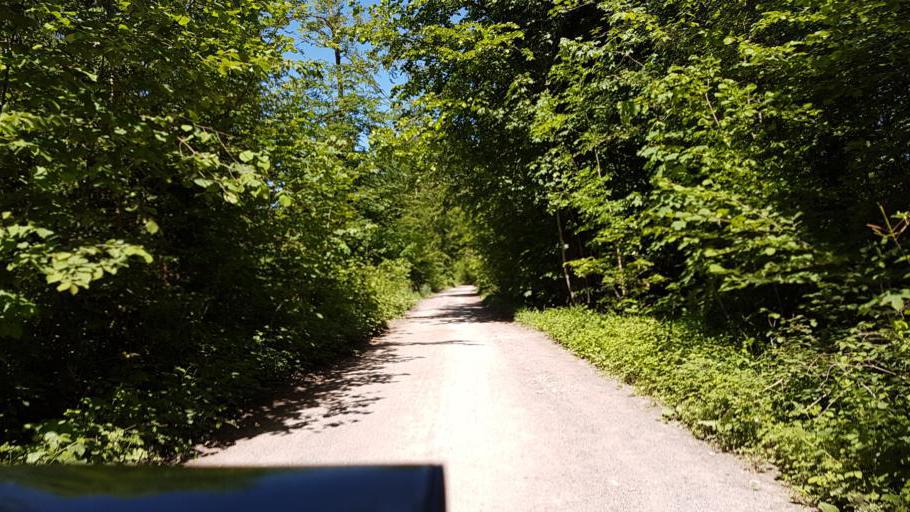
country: CH
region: Bern
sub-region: Thun District
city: Thun
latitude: 46.7136
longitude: 7.6178
